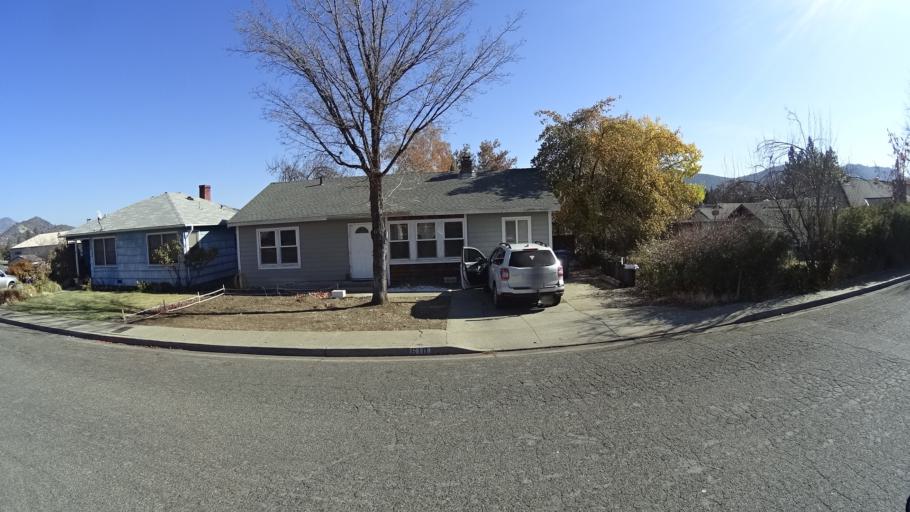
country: US
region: California
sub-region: Siskiyou County
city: Yreka
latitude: 41.7394
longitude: -122.6380
